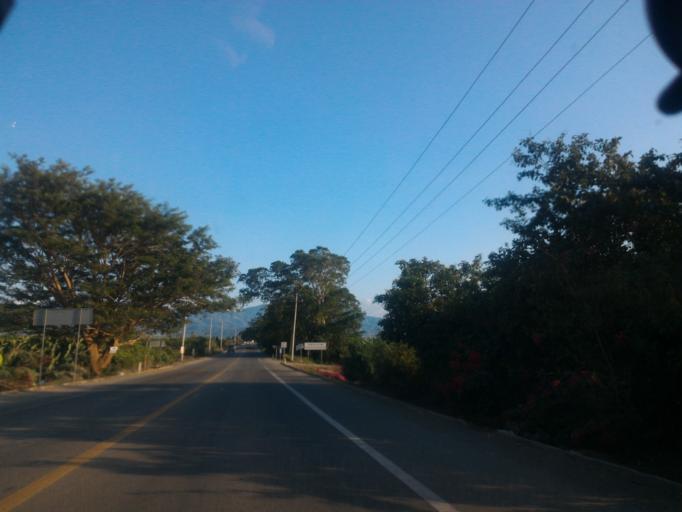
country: MX
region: Michoacan
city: Coahuayana Viejo
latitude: 18.7145
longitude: -103.7138
